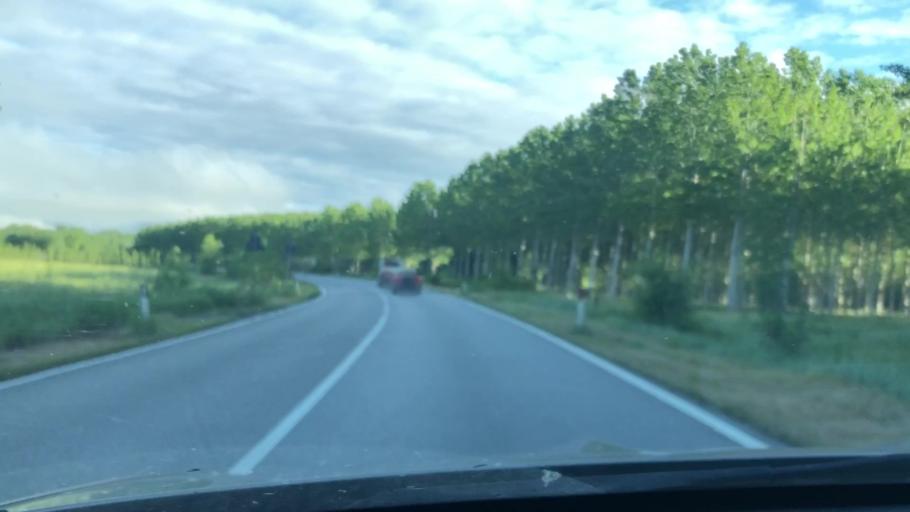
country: IT
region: Tuscany
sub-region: Province of Pisa
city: Forcoli
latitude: 43.6026
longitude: 10.6940
